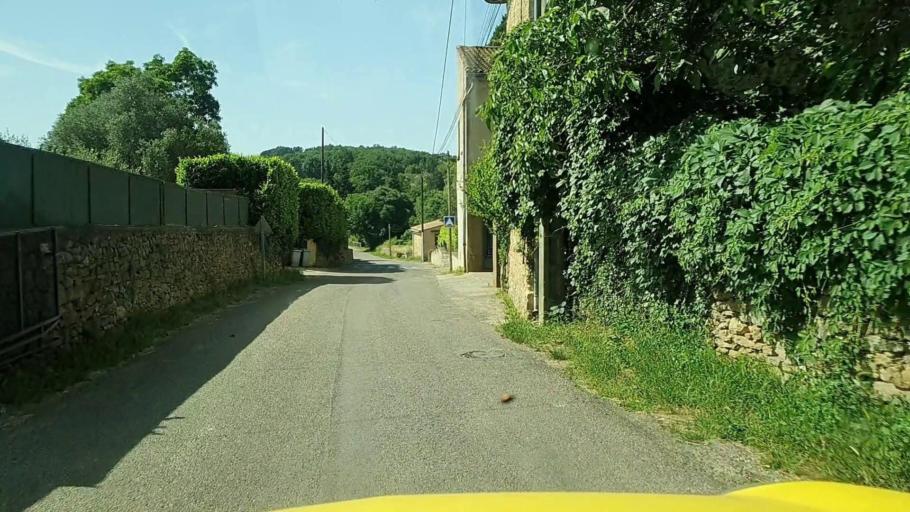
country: FR
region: Languedoc-Roussillon
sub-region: Departement du Gard
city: Sabran
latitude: 44.1420
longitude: 4.4897
